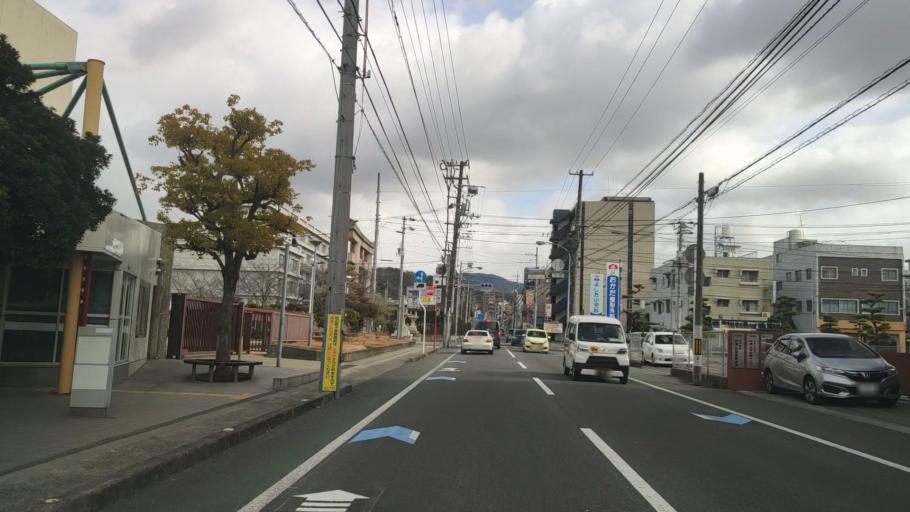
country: JP
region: Ehime
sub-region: Shikoku-chuo Shi
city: Matsuyama
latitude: 33.8523
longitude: 132.7730
